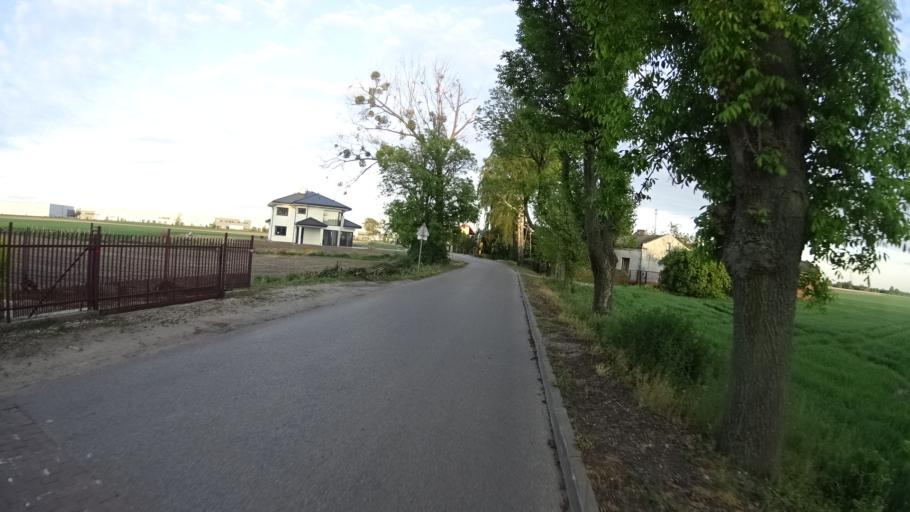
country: PL
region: Masovian Voivodeship
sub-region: Powiat warszawski zachodni
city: Ozarow Mazowiecki
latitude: 52.2039
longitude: 20.7588
